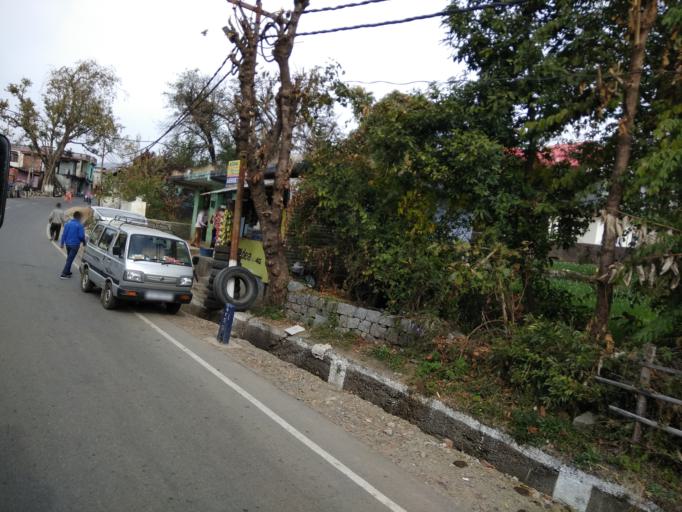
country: IN
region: Himachal Pradesh
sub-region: Kangra
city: Dharmsala
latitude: 32.1869
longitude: 76.3619
